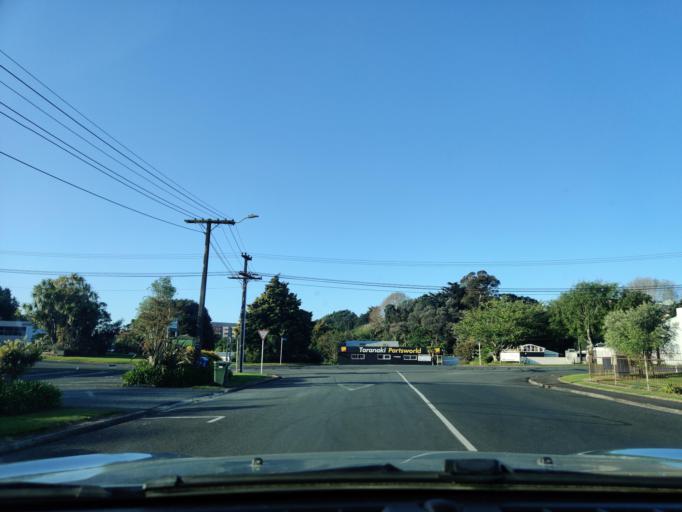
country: NZ
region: Taranaki
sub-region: New Plymouth District
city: New Plymouth
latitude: -39.0759
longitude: 174.0546
